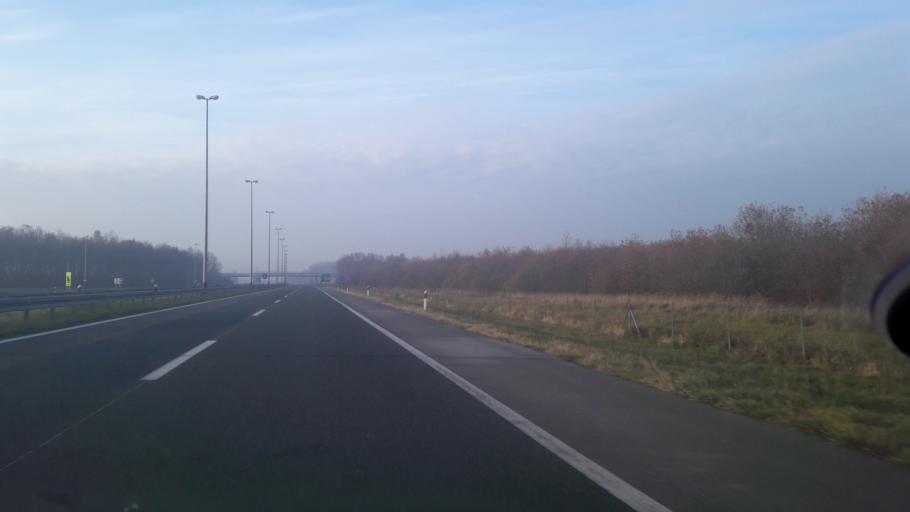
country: HR
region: Osjecko-Baranjska
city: Vuka
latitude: 45.4756
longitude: 18.4860
